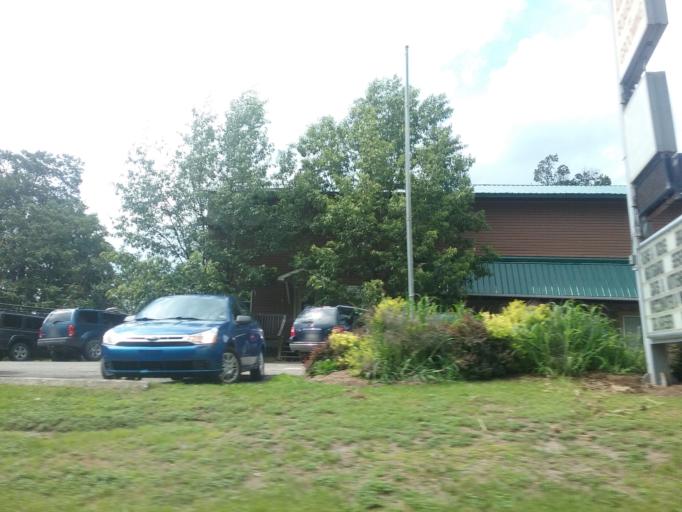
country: US
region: Pennsylvania
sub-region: Tioga County
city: Wellsboro
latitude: 41.7476
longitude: -77.2469
